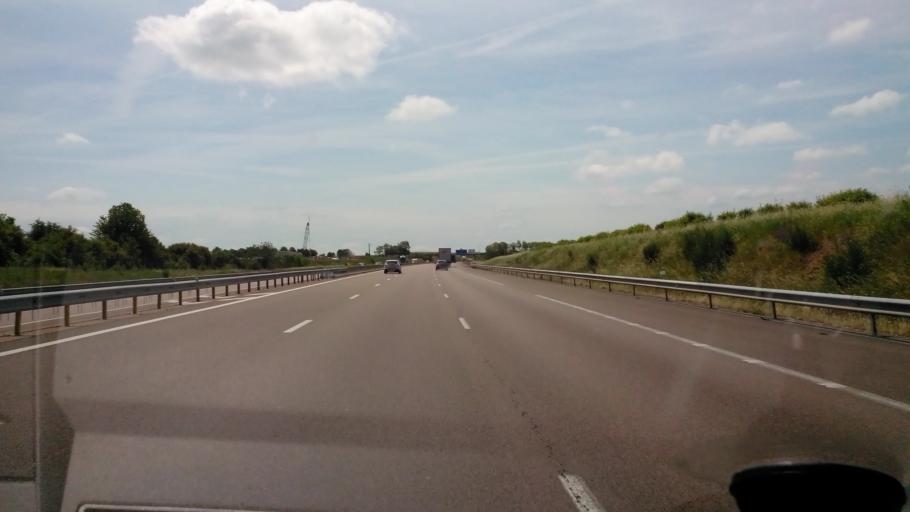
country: FR
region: Champagne-Ardenne
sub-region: Departement de la Haute-Marne
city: Langres
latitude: 47.8028
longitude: 5.2245
